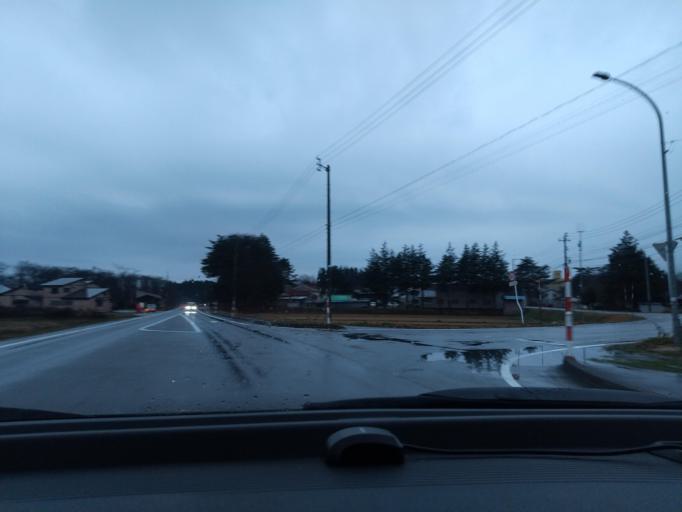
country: JP
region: Akita
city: Kakunodatemachi
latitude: 39.6114
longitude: 140.6263
